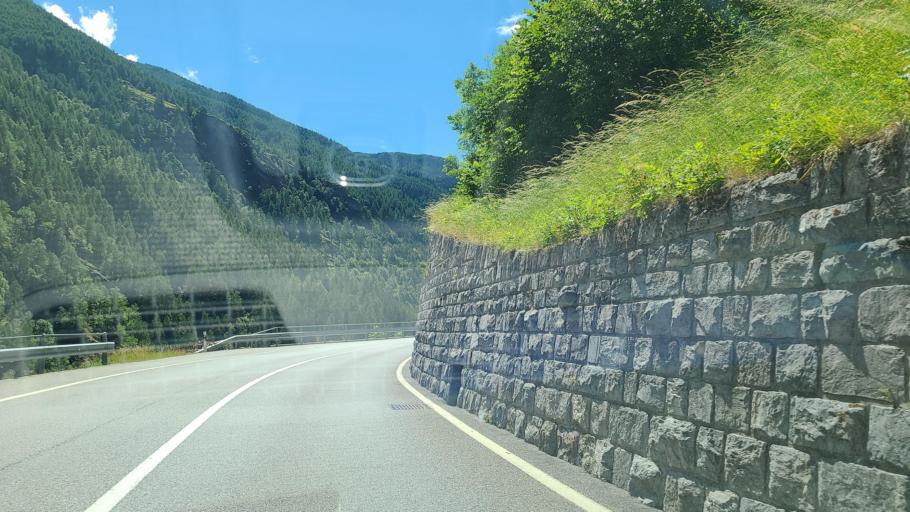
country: CH
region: Valais
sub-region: Visp District
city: Stalden
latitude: 46.1972
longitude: 7.8954
